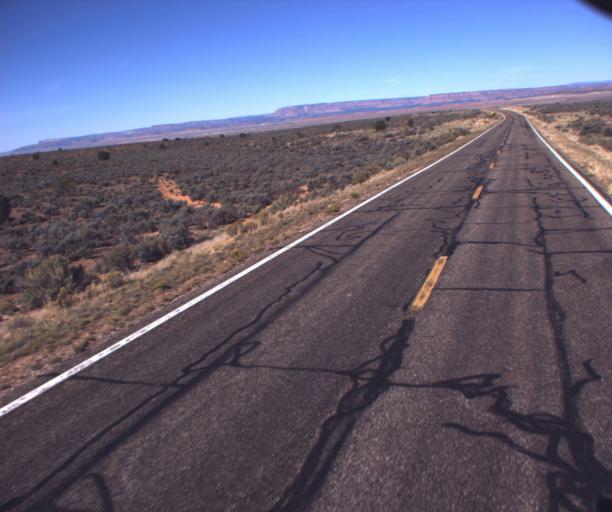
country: US
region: Arizona
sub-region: Coconino County
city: Fredonia
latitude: 36.8875
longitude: -112.3489
